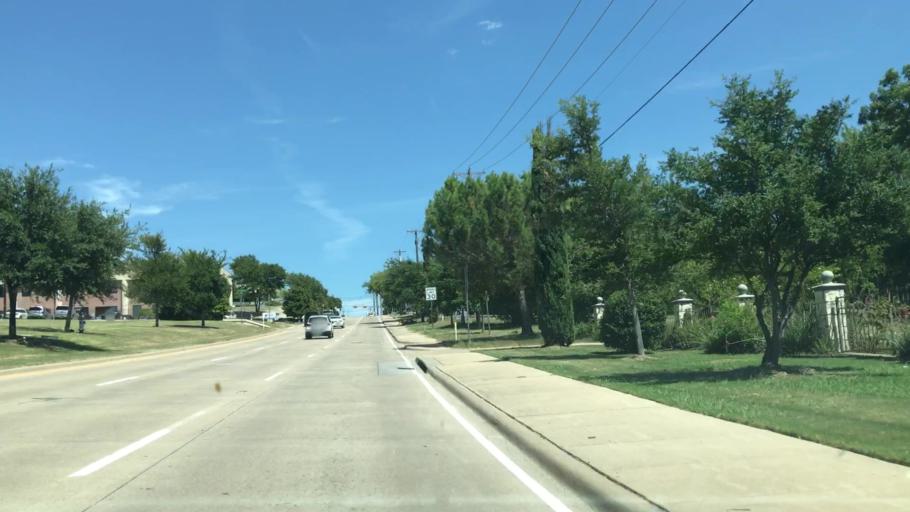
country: US
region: Texas
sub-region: Rockwall County
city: Rockwall
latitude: 32.9304
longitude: -96.4645
